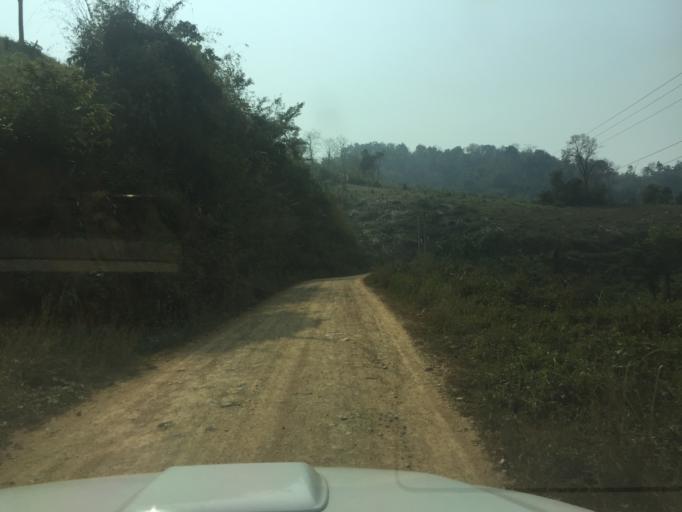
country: TH
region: Phayao
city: Phu Sang
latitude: 19.6239
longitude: 100.5389
